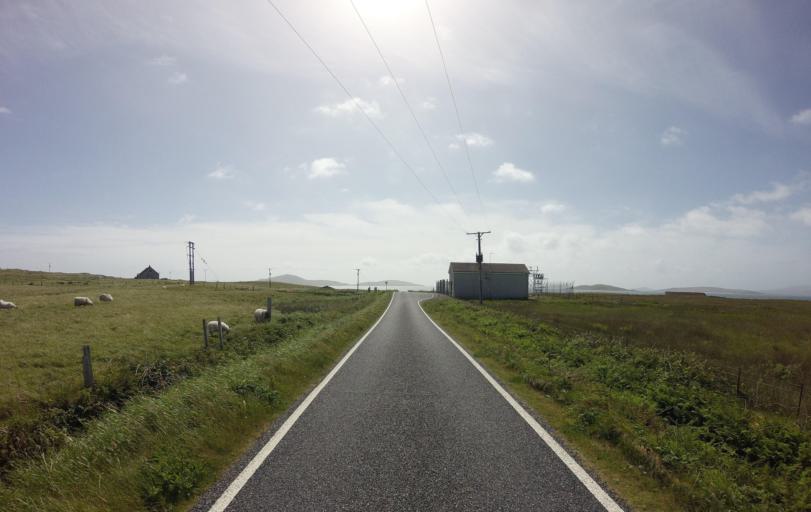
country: GB
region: Scotland
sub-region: Eilean Siar
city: Isle of South Uist
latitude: 57.1070
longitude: -7.3692
